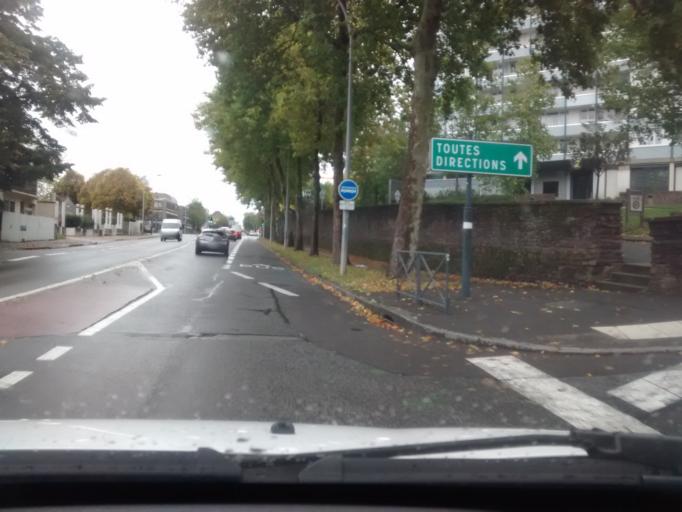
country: FR
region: Brittany
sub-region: Departement d'Ille-et-Vilaine
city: Rennes
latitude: 48.1272
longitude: -1.6649
